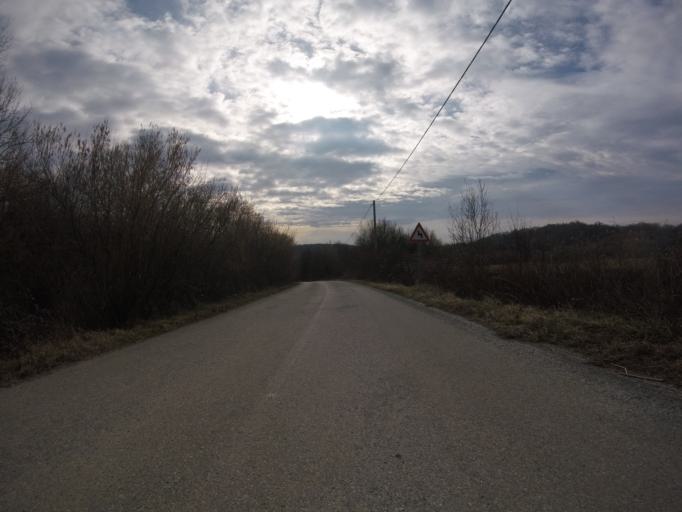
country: HR
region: Sisacko-Moslavacka
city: Glina
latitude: 45.4750
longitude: 16.0248
